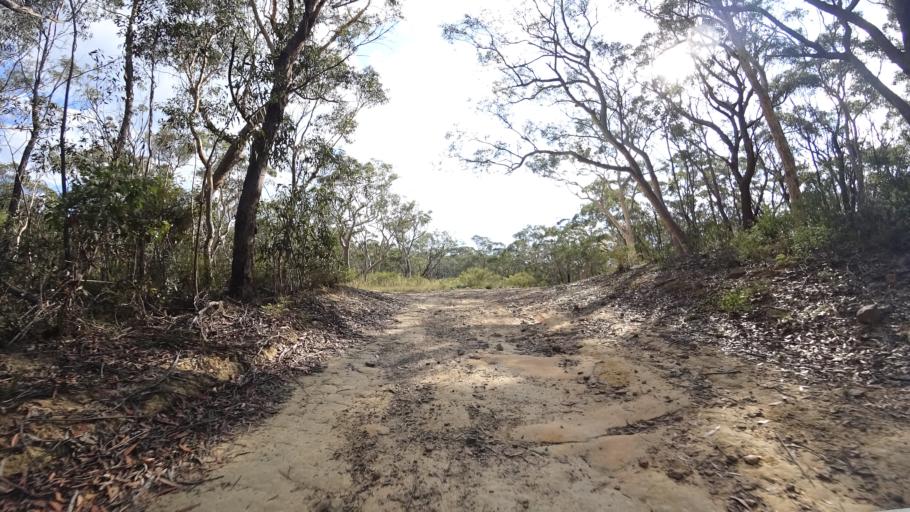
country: AU
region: New South Wales
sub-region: Lithgow
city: Lithgow
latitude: -33.3359
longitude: 150.2835
